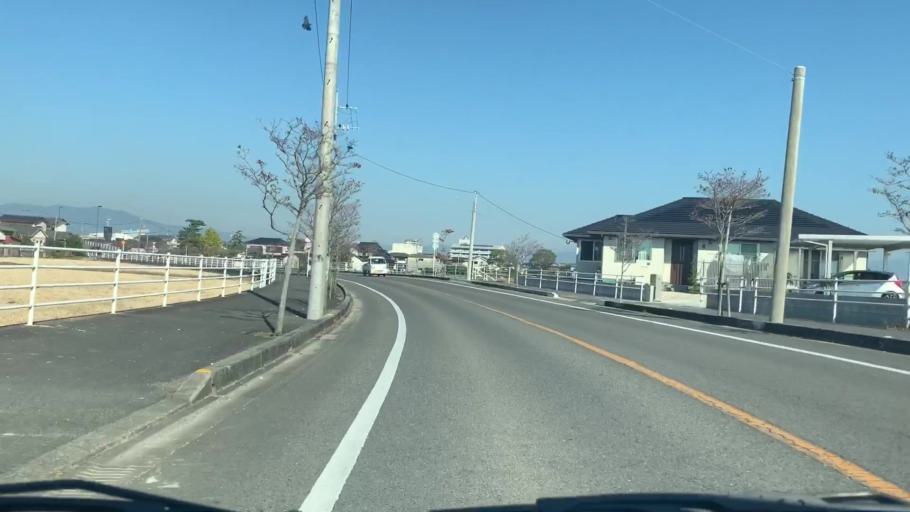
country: JP
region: Saga Prefecture
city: Saga-shi
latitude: 33.2344
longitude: 130.3128
